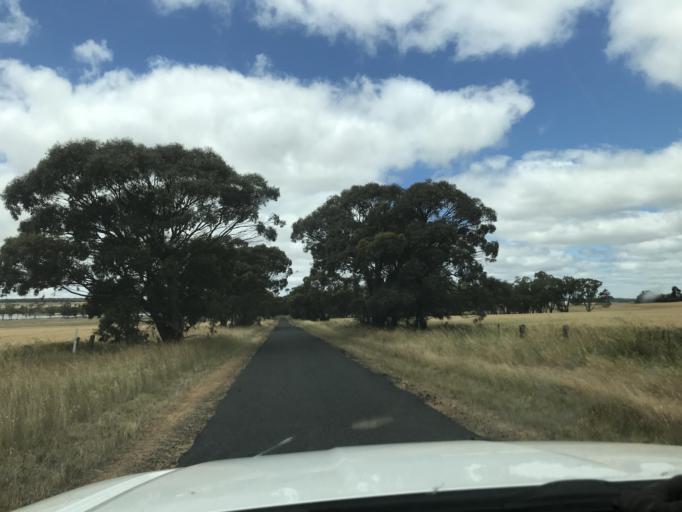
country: AU
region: South Australia
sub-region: Tatiara
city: Bordertown
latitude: -36.3621
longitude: 141.3993
